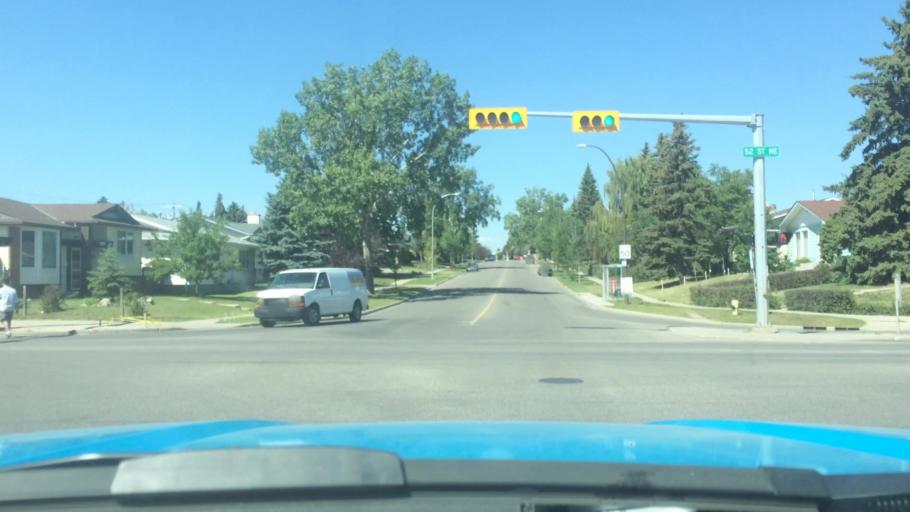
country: CA
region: Alberta
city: Calgary
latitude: 51.0859
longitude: -113.9583
